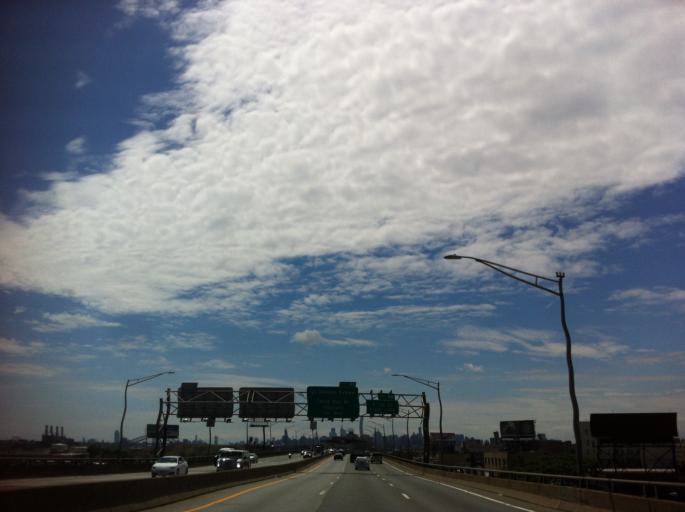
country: US
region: New York
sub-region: Bronx
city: The Bronx
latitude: 40.8127
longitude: -73.8984
